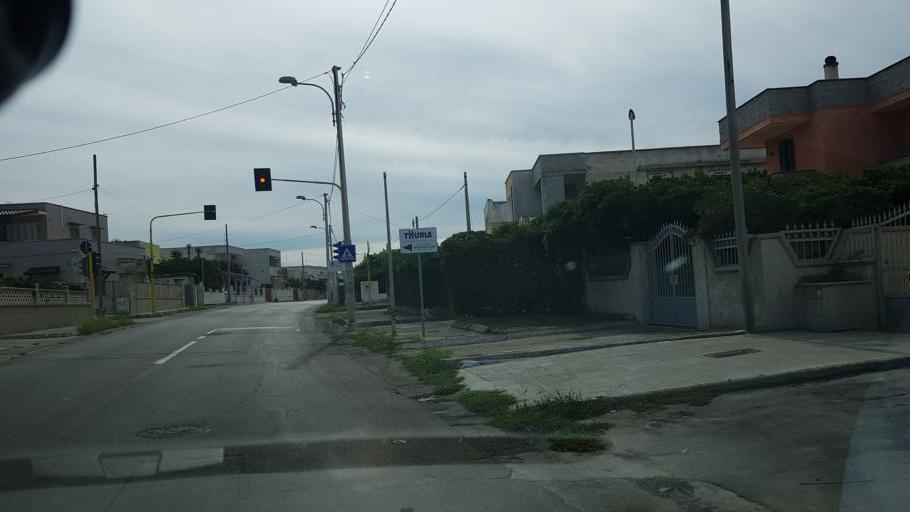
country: IT
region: Apulia
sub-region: Provincia di Lecce
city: Borgagne
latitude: 40.2932
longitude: 18.4211
